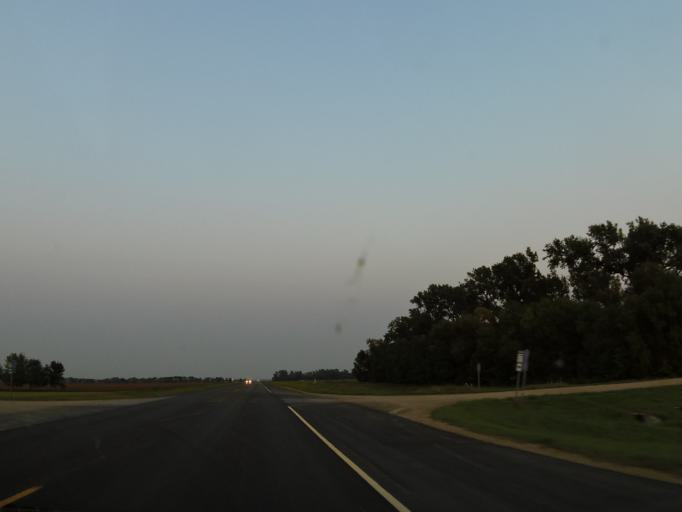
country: US
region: North Dakota
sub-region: Walsh County
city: Grafton
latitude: 48.4126
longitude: -97.5363
